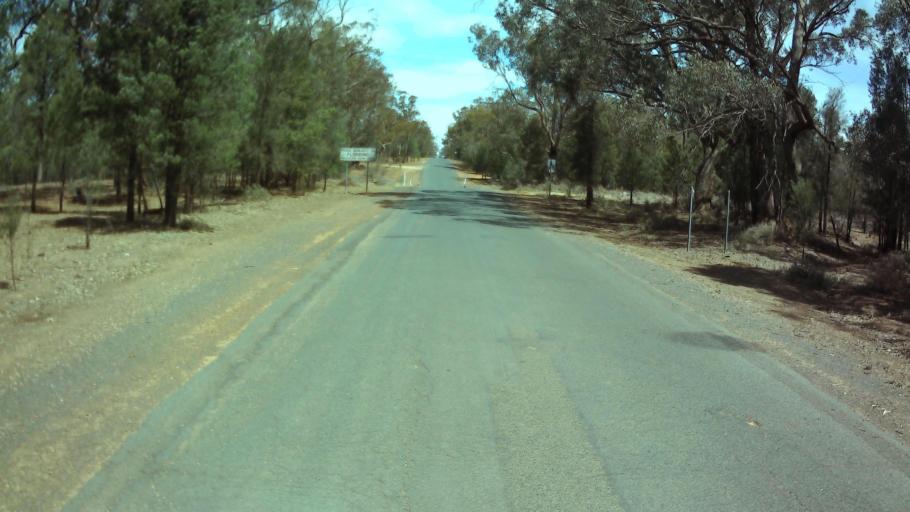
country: AU
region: New South Wales
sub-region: Weddin
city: Grenfell
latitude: -33.8474
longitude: 147.7434
